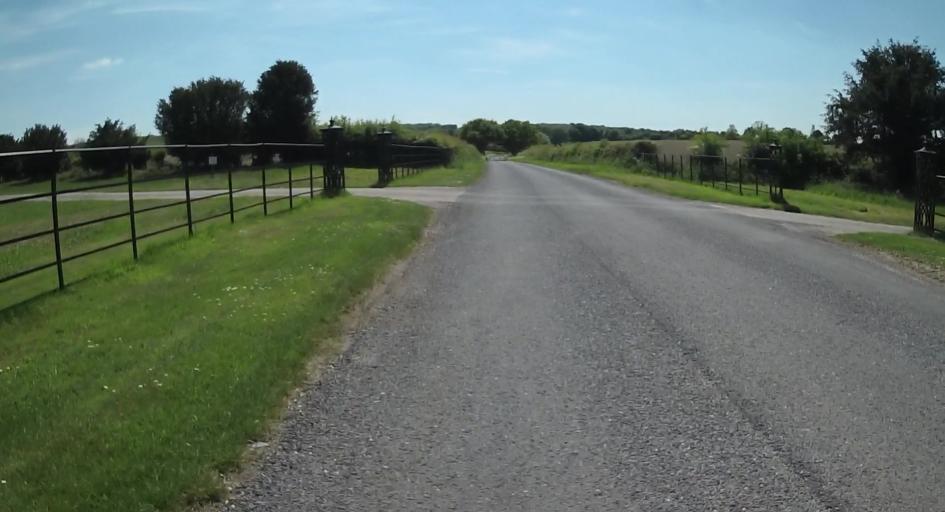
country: GB
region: England
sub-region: Hampshire
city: Four Marks
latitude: 51.1501
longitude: -1.1461
